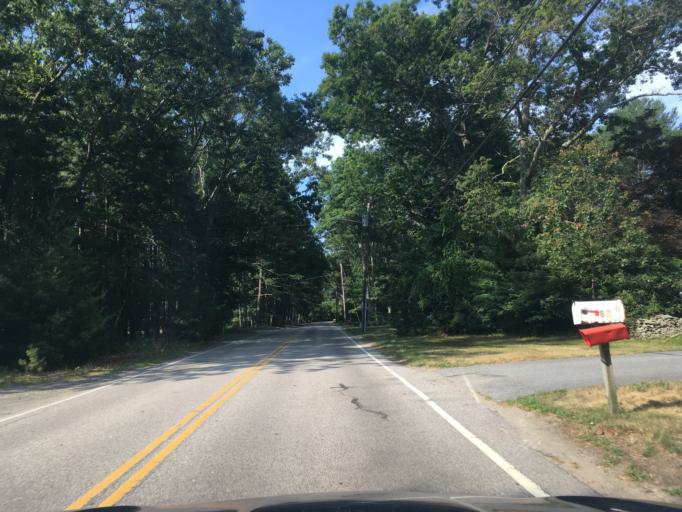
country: US
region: Rhode Island
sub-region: Kent County
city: East Greenwich
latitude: 41.6202
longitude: -71.4334
